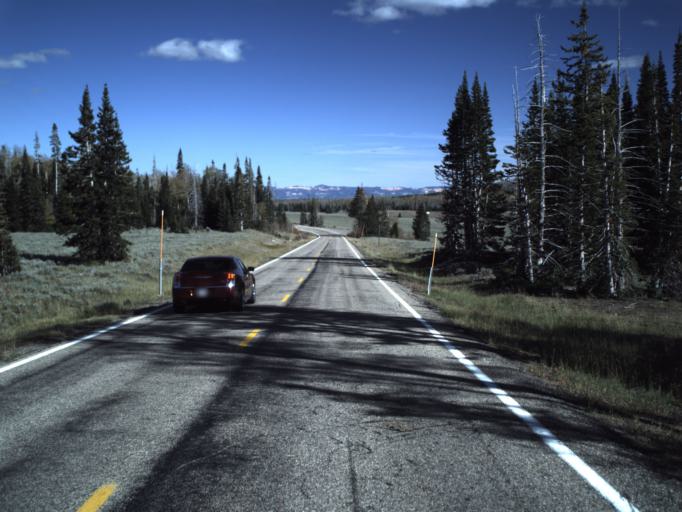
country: US
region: Utah
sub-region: Iron County
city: Parowan
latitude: 37.6510
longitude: -112.7935
